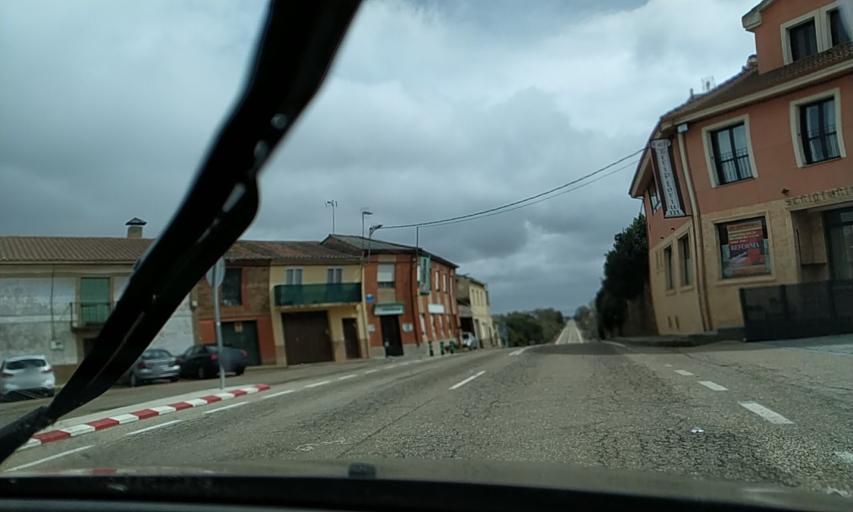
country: ES
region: Castille and Leon
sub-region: Provincia de Zamora
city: Tabara
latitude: 41.8266
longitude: -5.9586
